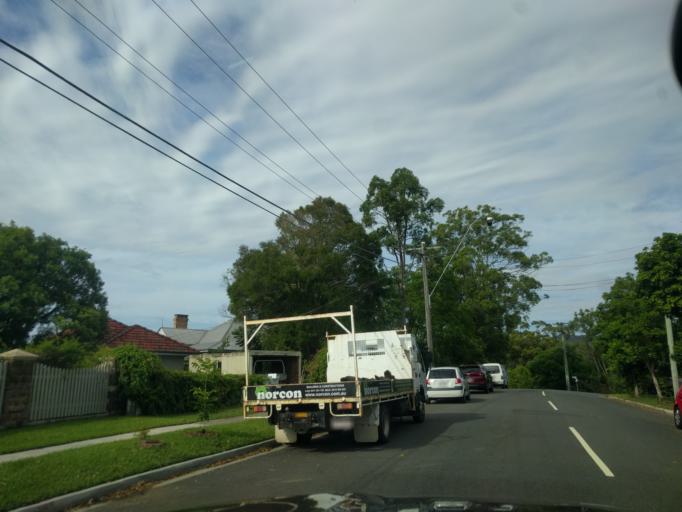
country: AU
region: Queensland
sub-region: Brisbane
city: Toowong
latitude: -27.4706
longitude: 152.9880
